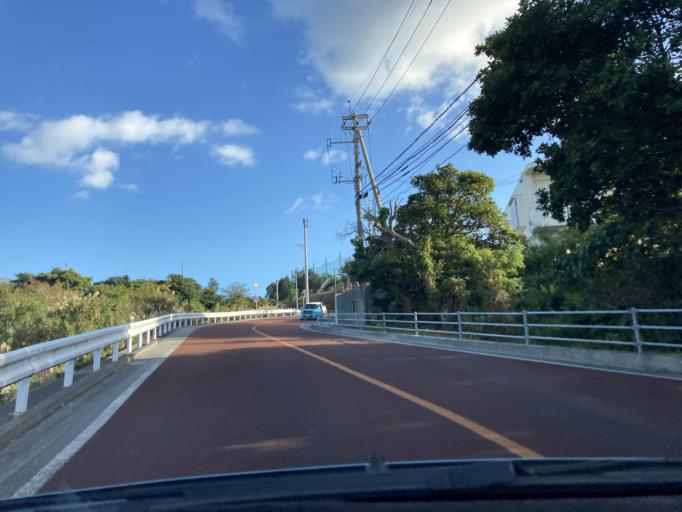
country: JP
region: Okinawa
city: Chatan
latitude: 26.2951
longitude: 127.7997
